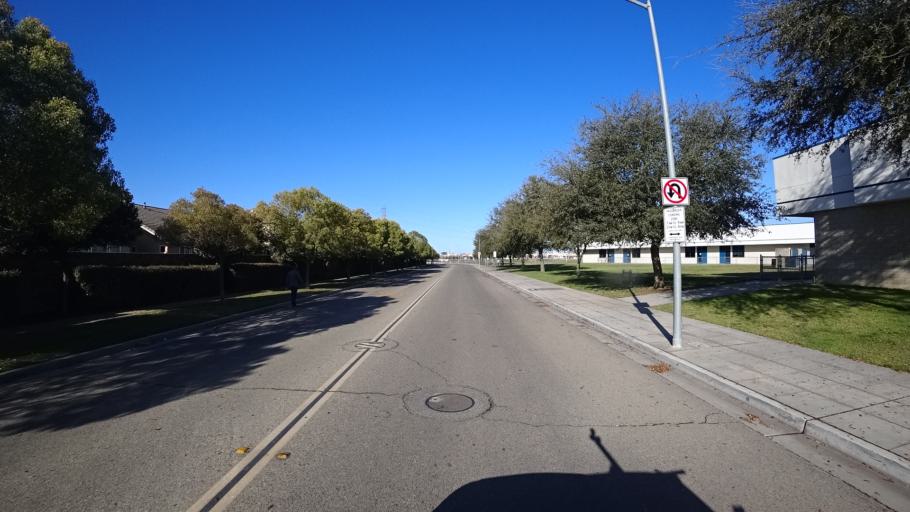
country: US
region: California
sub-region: Fresno County
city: Biola
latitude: 36.8334
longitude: -119.9054
